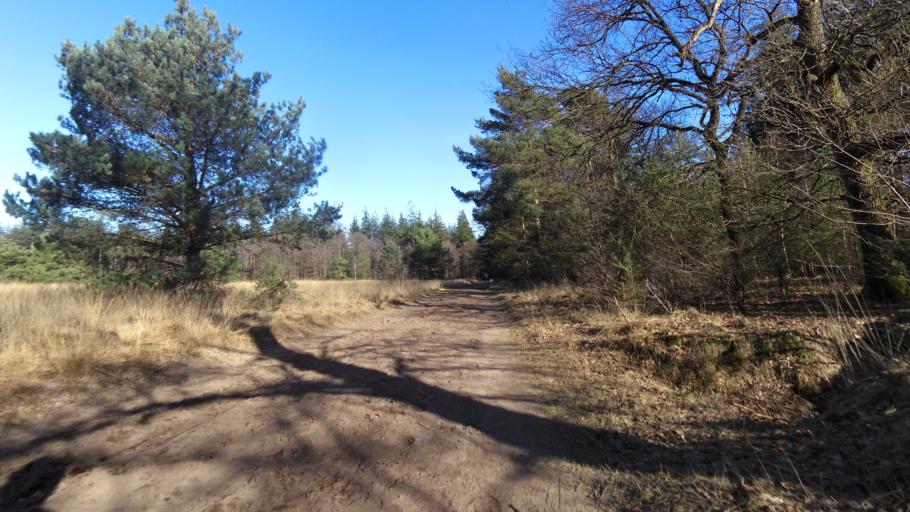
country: NL
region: Gelderland
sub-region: Gemeente Barneveld
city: Stroe
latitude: 52.2120
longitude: 5.6832
